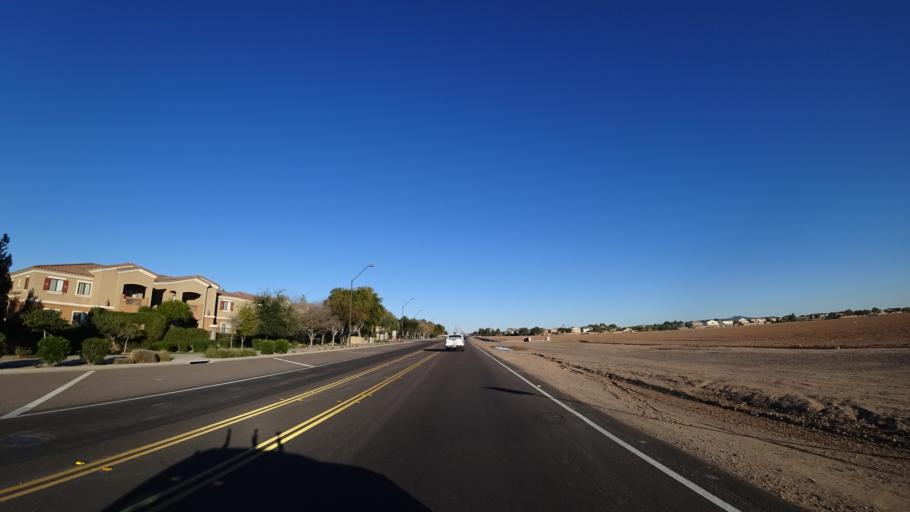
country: US
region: Arizona
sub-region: Maricopa County
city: Tolleson
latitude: 33.4497
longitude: -112.3026
